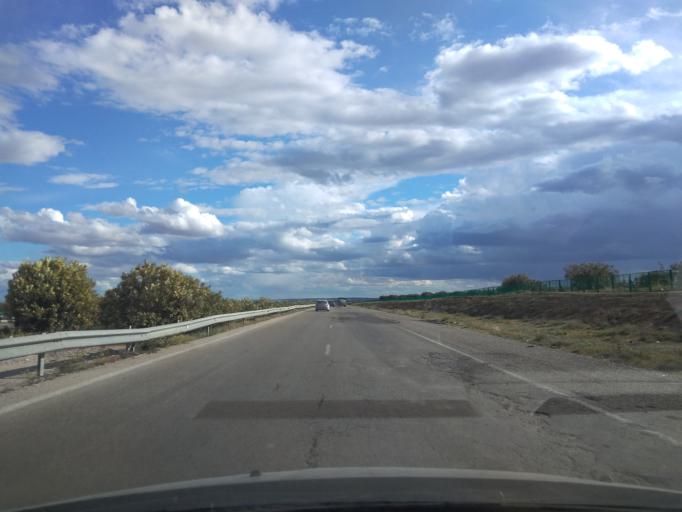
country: TN
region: Al Munastir
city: Manzil Kamil
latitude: 35.5463
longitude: 10.6209
